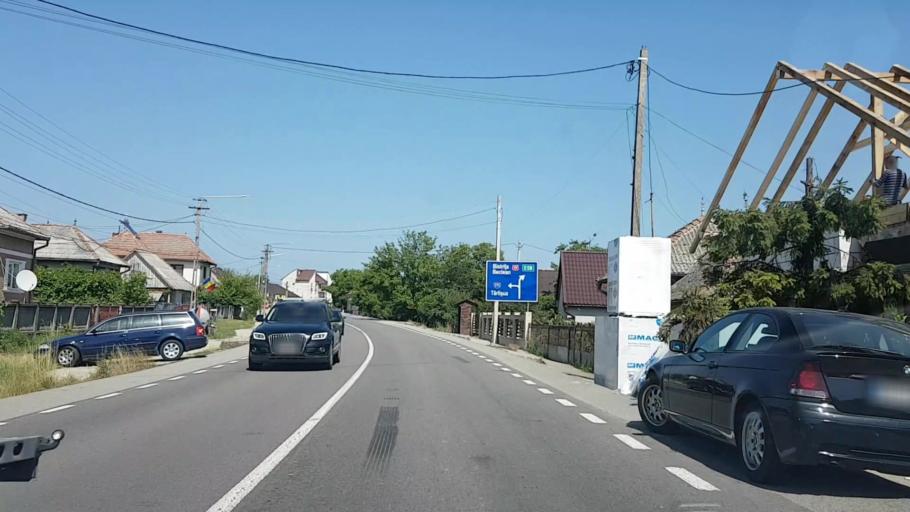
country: RO
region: Bistrita-Nasaud
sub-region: Comuna Uriu
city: Uriu
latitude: 47.2012
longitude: 24.0594
